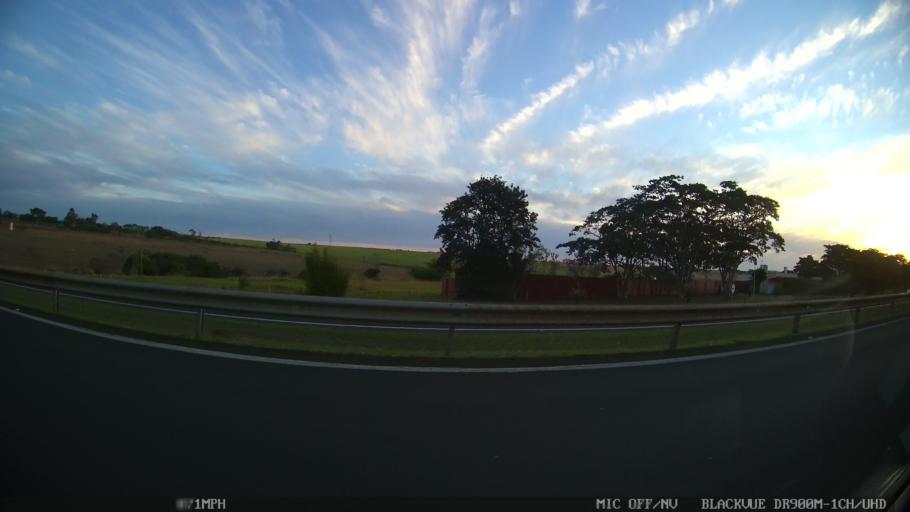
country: BR
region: Sao Paulo
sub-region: Pindorama
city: Pindorama
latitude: -21.1985
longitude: -48.9423
